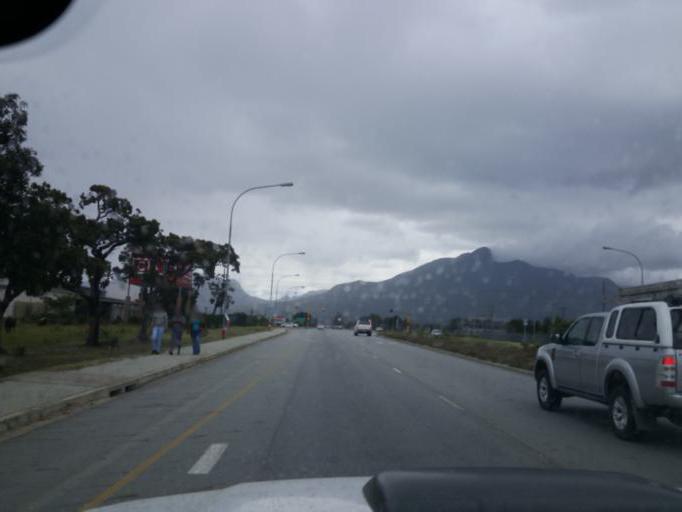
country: ZA
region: Western Cape
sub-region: Eden District Municipality
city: George
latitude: -33.9795
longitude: 22.4967
